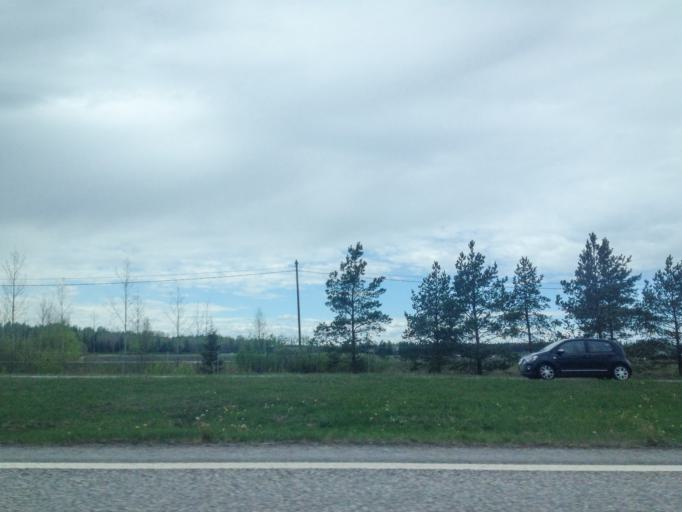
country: FI
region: Uusimaa
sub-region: Helsinki
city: Nurmijaervi
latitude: 60.5116
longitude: 24.8482
